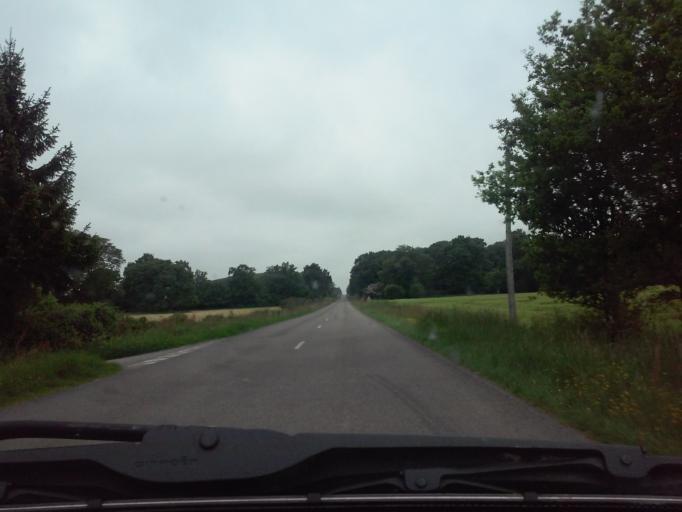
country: FR
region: Brittany
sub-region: Departement d'Ille-et-Vilaine
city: Le Pertre
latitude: 47.9622
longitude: -1.0056
